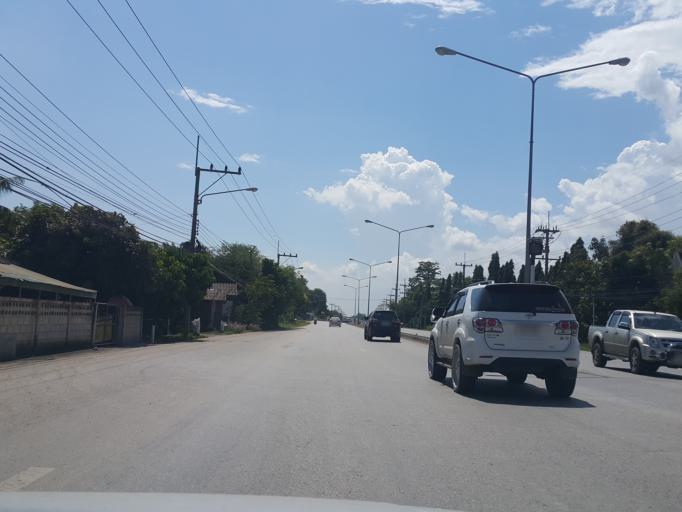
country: TH
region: Chiang Mai
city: Mae Taeng
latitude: 19.0448
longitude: 98.9467
